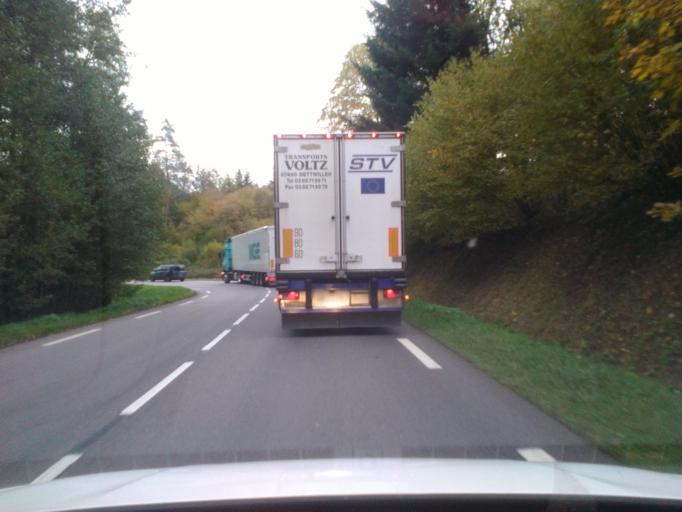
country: FR
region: Lorraine
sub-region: Departement des Vosges
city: Ban-de-Laveline
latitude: 48.3370
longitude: 7.1044
